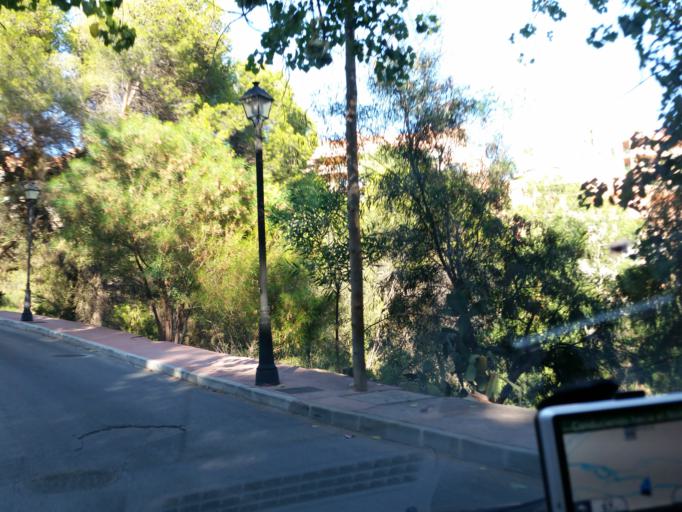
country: ES
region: Andalusia
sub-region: Provincia de Malaga
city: Fuengirola
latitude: 36.5719
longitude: -4.6061
